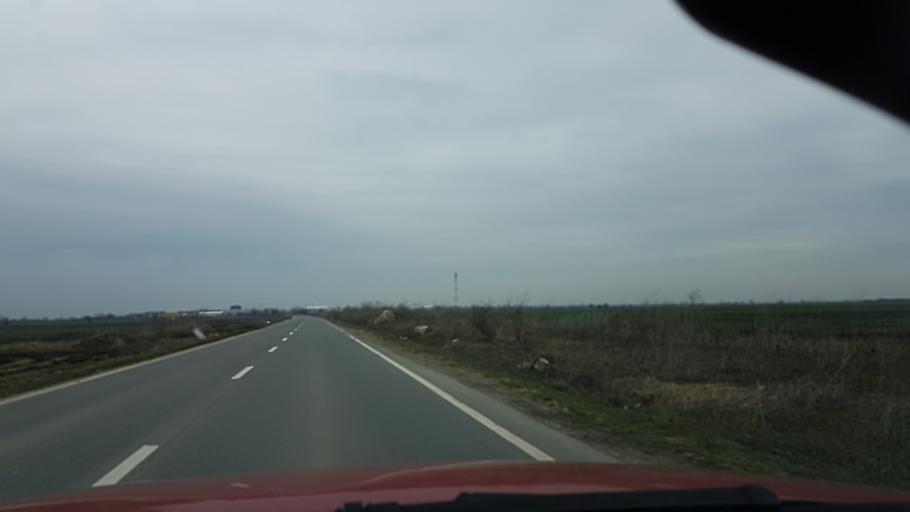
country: RO
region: Ilfov
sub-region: Comuna Balotesti
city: Balotesti
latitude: 44.6035
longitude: 26.1310
